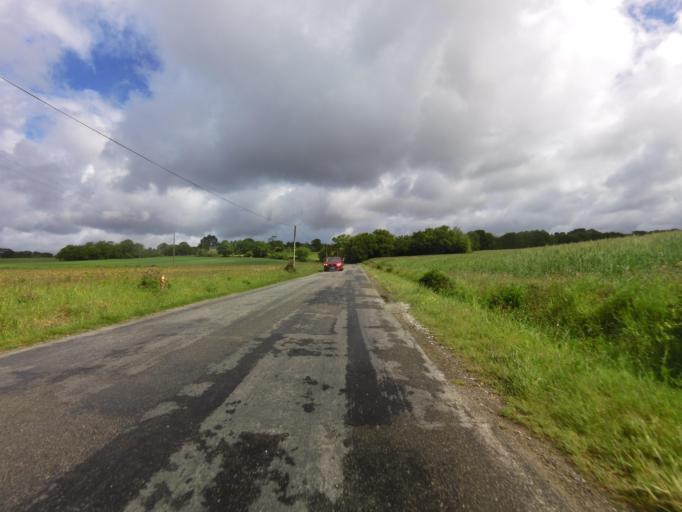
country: FR
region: Brittany
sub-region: Departement du Morbihan
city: Plougoumelen
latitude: 47.6525
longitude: -2.9014
